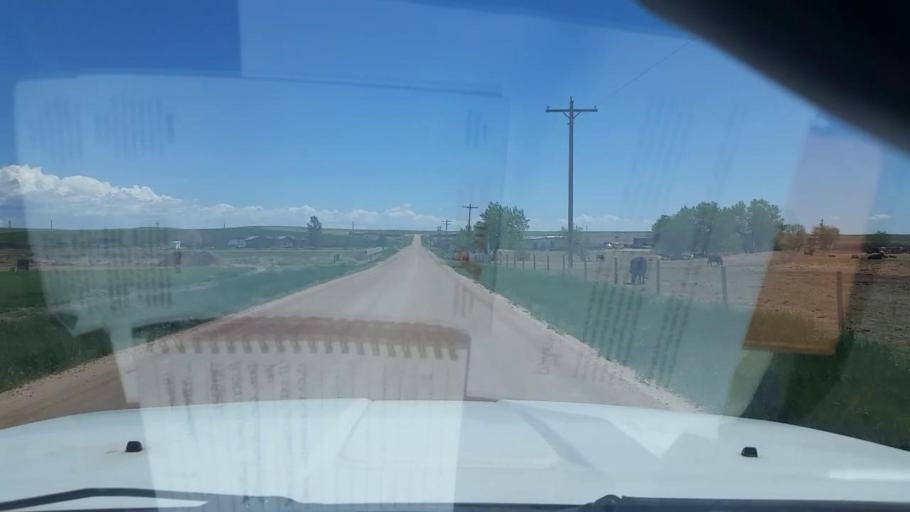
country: US
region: Colorado
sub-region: Larimer County
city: Wellington
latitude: 40.7981
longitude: -105.0507
